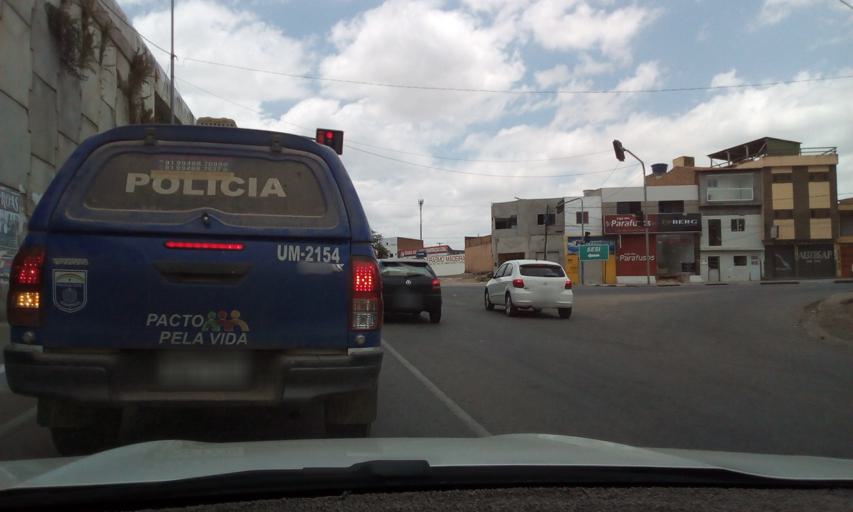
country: BR
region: Pernambuco
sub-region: Caruaru
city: Caruaru
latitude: -8.2764
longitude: -35.9818
